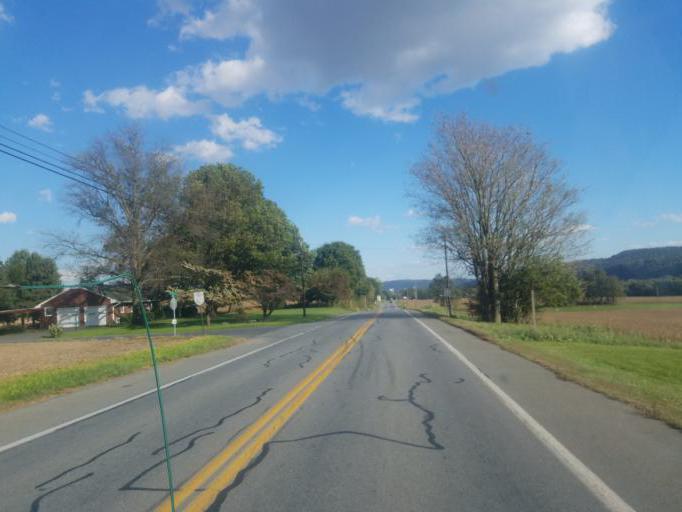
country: US
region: Pennsylvania
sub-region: Lancaster County
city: Maytown
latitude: 40.0694
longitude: -76.6250
